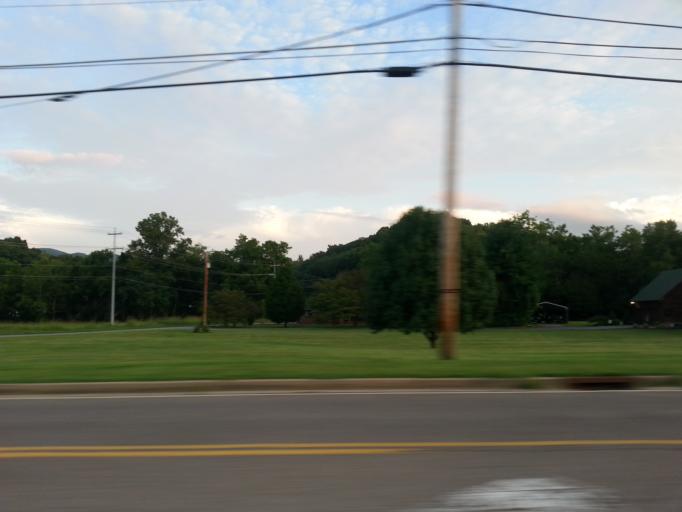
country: US
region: Tennessee
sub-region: Carter County
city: Hunter
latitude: 36.4012
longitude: -82.1034
